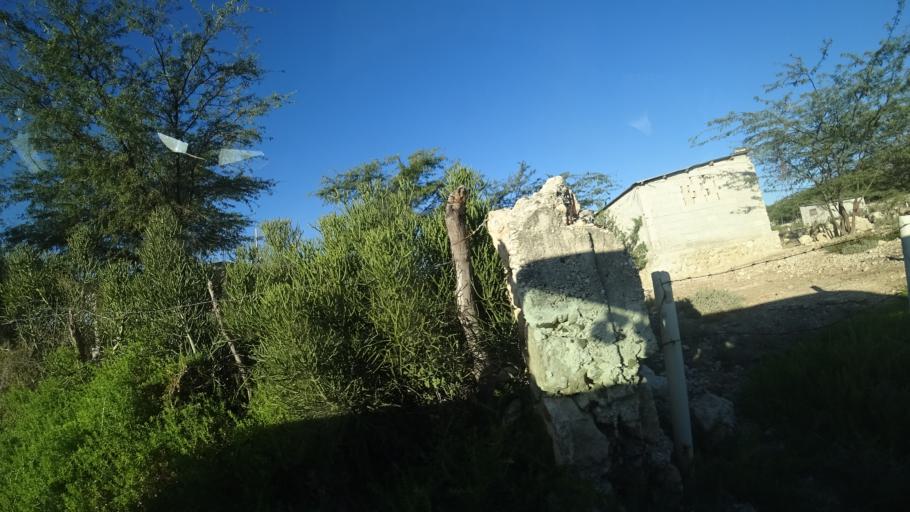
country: HT
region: Ouest
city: Croix des Bouquets
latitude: 18.6603
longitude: -72.2229
